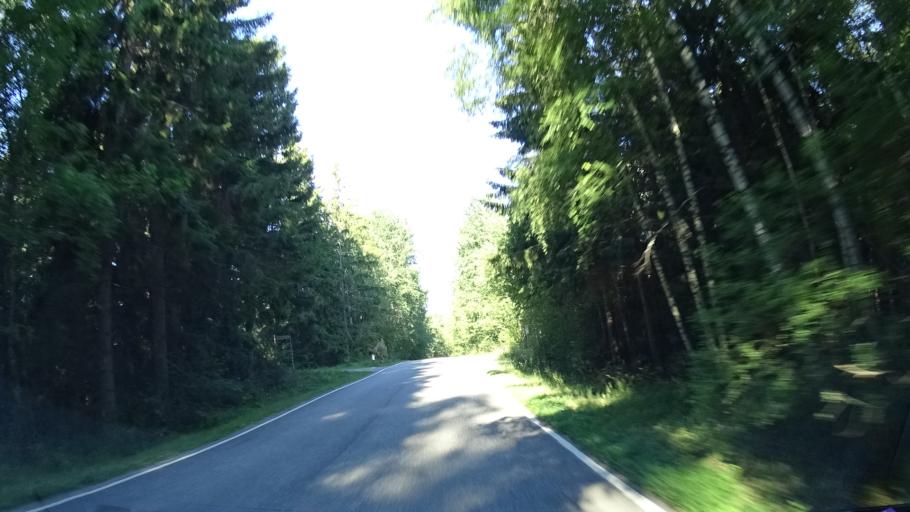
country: FI
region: Varsinais-Suomi
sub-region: Turku
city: Merimasku
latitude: 60.4977
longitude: 21.7838
